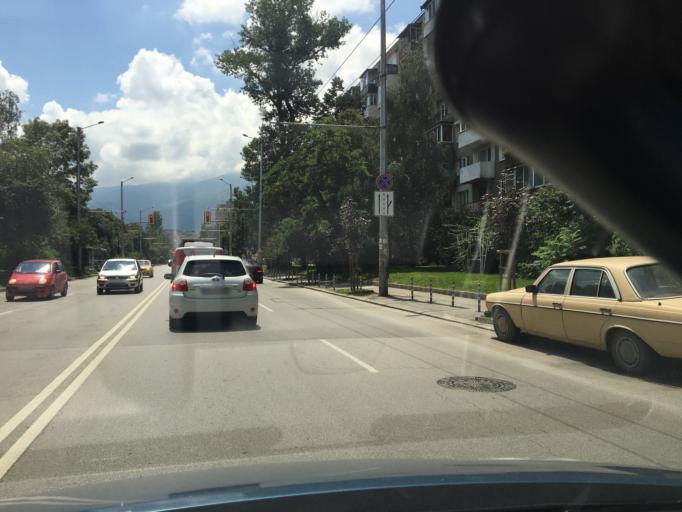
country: BG
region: Sofia-Capital
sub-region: Stolichna Obshtina
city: Sofia
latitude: 42.6706
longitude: 23.3039
